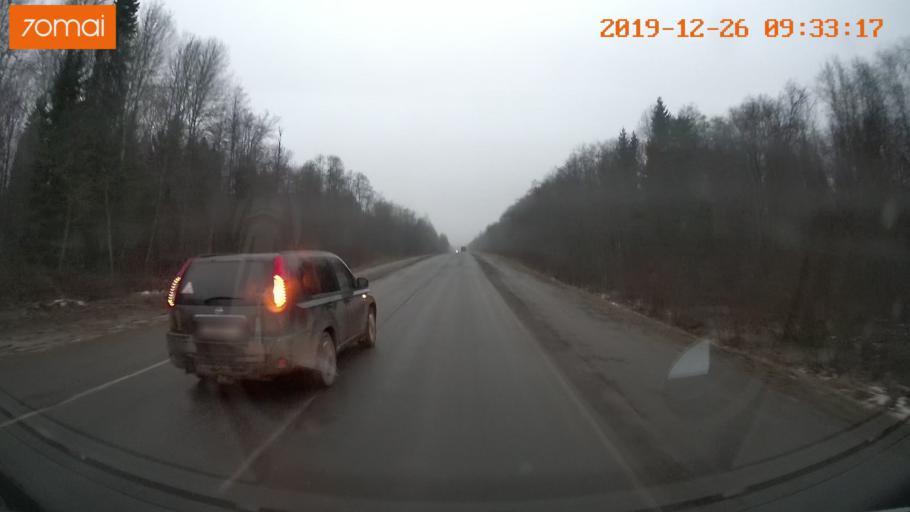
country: RU
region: Vologda
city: Gryazovets
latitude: 59.0882
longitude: 40.1035
